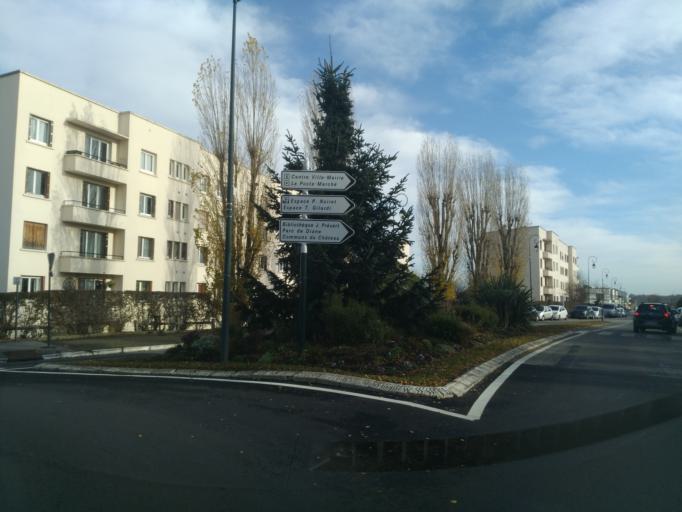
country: FR
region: Ile-de-France
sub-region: Departement des Yvelines
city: Les Clayes-sous-Bois
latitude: 48.8232
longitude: 1.9840
